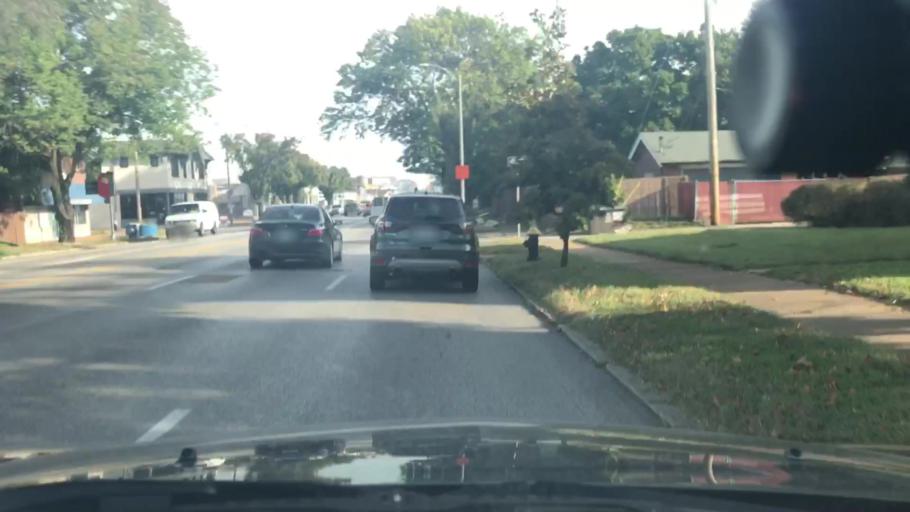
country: US
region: Missouri
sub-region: Saint Louis County
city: Richmond Heights
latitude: 38.6107
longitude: -90.2680
